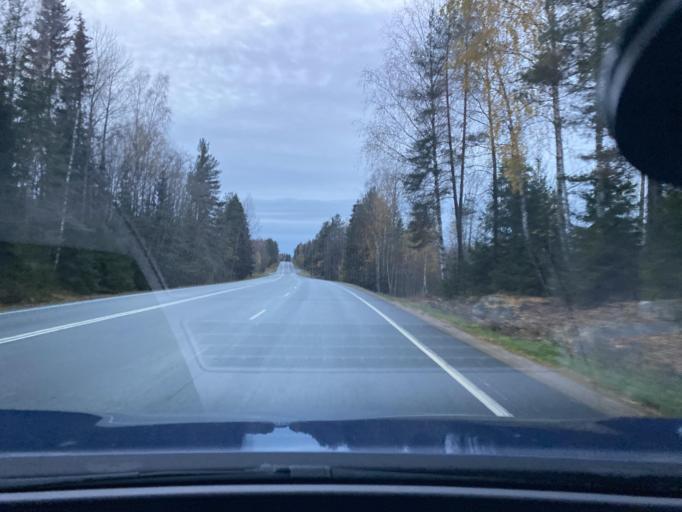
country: FI
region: Uusimaa
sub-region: Helsinki
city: Sammatti
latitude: 60.3862
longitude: 23.8574
